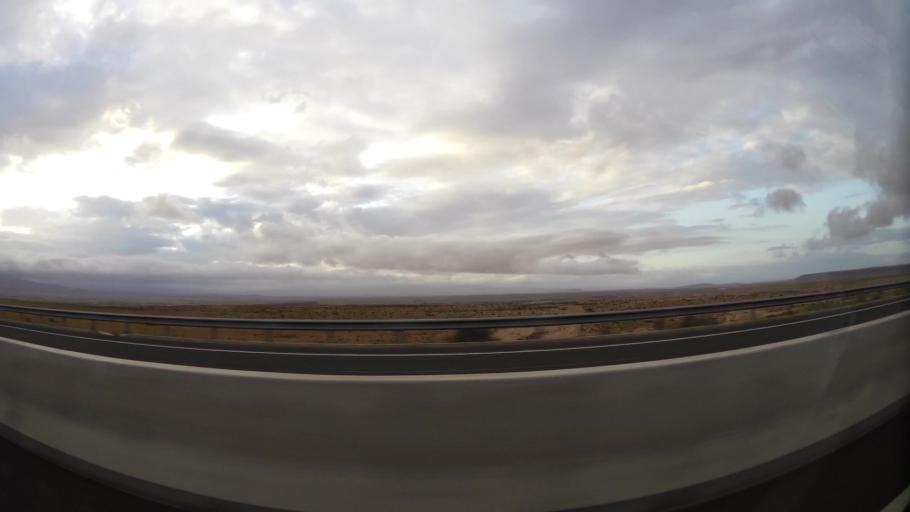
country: MA
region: Oriental
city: Taourirt
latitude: 34.4140
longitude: -3.1353
